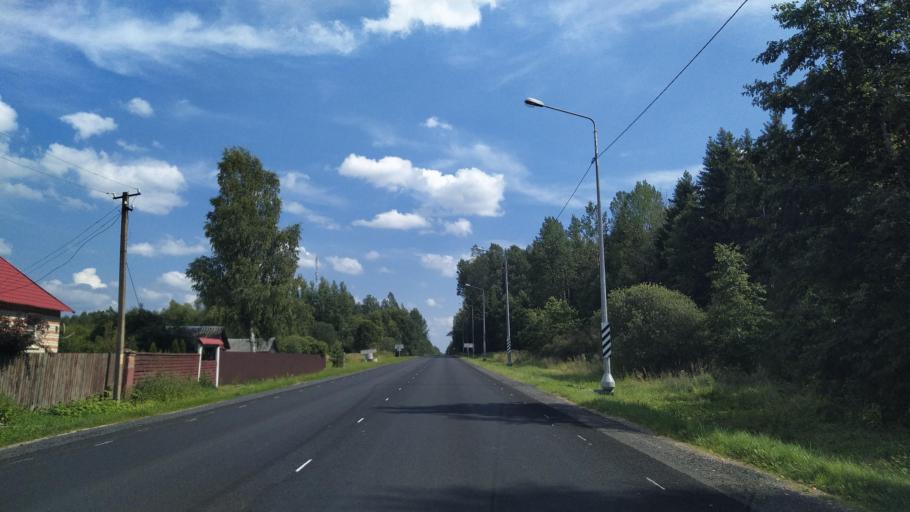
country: RU
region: Pskov
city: Porkhov
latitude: 57.7255
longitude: 29.1717
